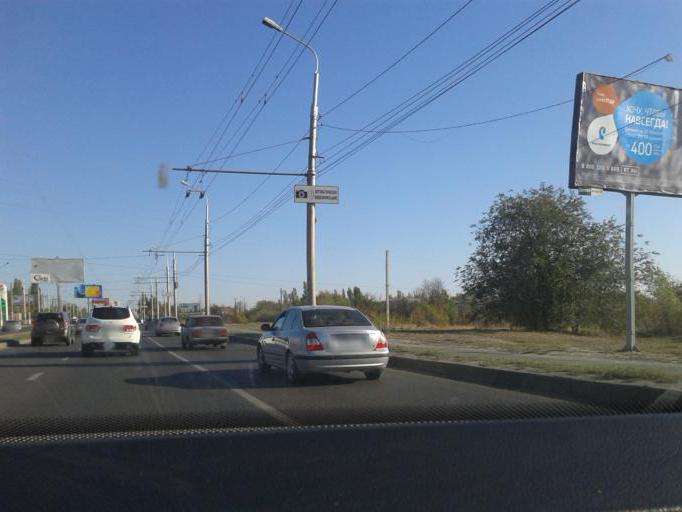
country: RU
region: Volgograd
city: Volgograd
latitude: 48.6431
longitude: 44.4326
